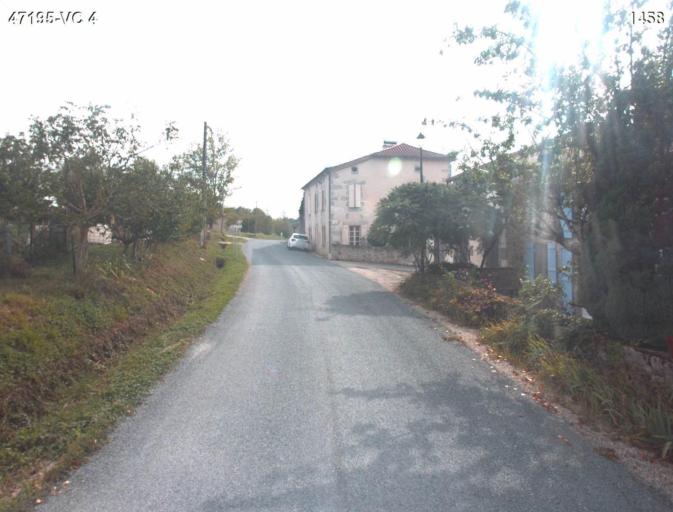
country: FR
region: Aquitaine
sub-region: Departement du Lot-et-Garonne
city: Nerac
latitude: 44.1090
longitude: 0.3832
